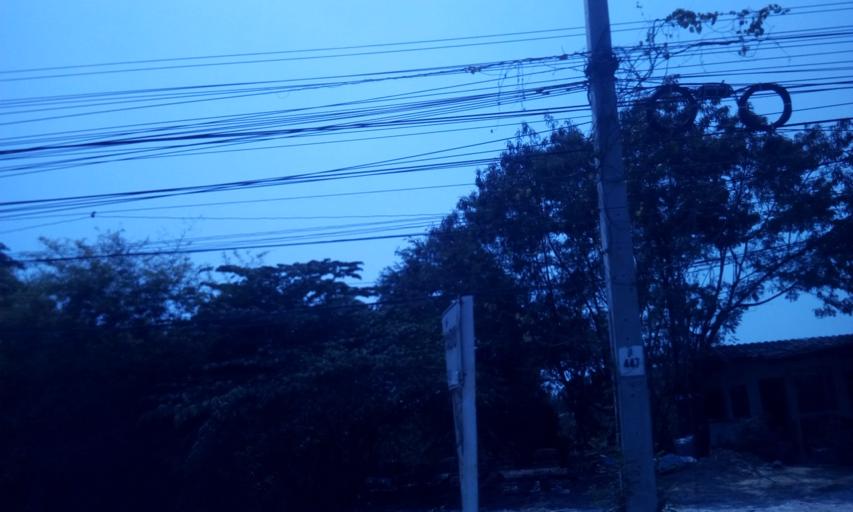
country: TH
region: Nonthaburi
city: Sai Noi
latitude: 13.9209
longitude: 100.3208
